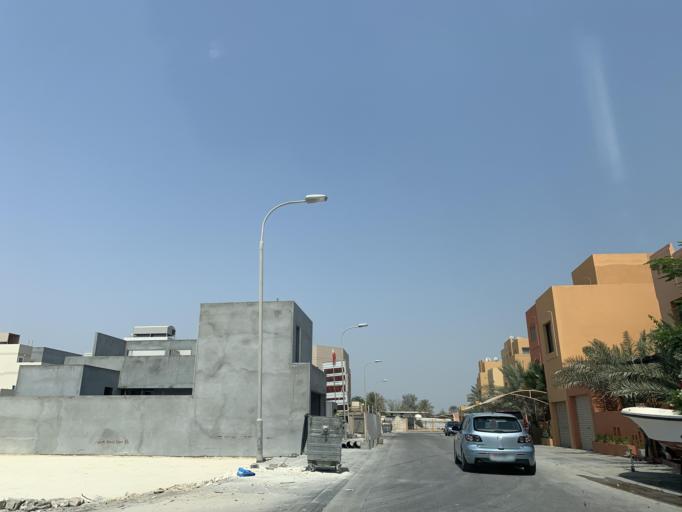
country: BH
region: Manama
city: Jidd Hafs
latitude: 26.2087
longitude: 50.5219
